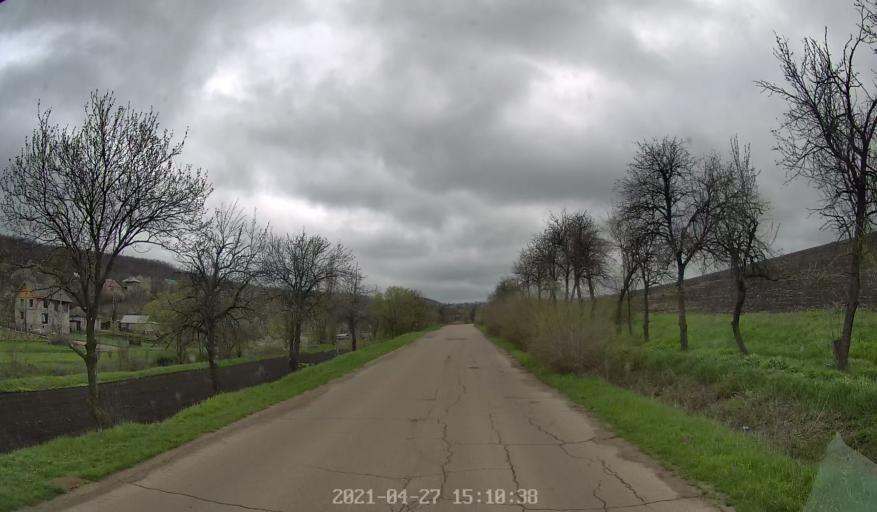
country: MD
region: Chisinau
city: Vadul lui Voda
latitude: 47.0386
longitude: 29.0324
